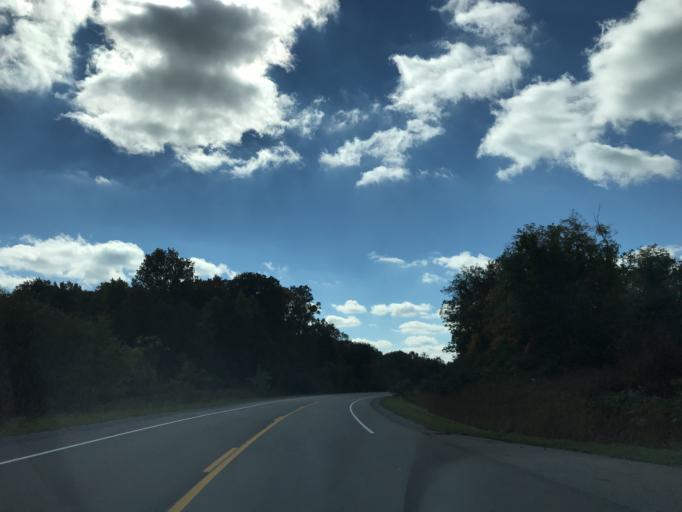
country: US
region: Michigan
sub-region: Washtenaw County
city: Ann Arbor
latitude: 42.3043
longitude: -83.6769
